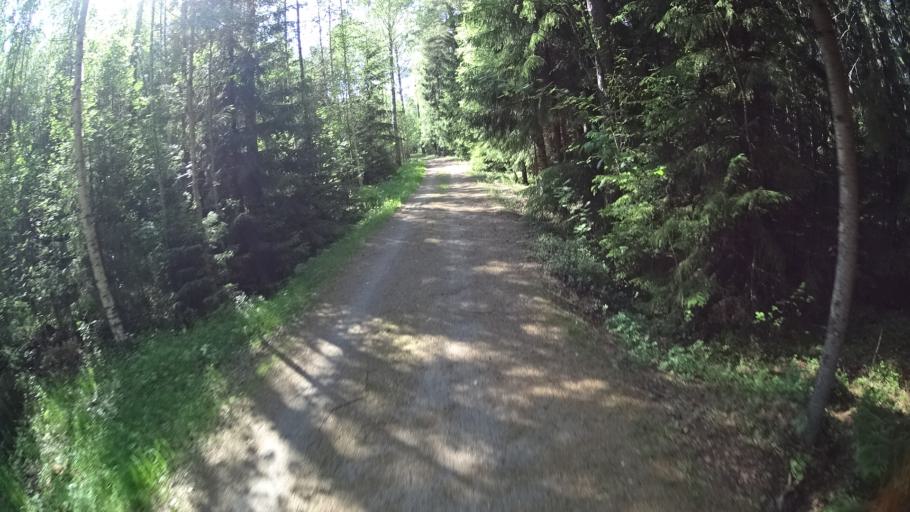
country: FI
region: Uusimaa
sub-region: Helsinki
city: Vantaa
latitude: 60.2355
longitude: 25.1782
